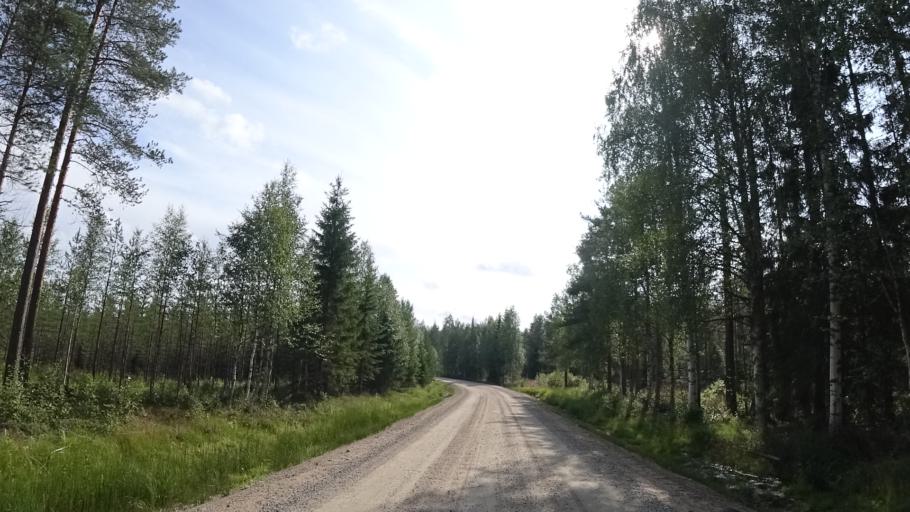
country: FI
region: North Karelia
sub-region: Pielisen Karjala
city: Lieksa
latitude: 63.5921
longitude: 30.1365
